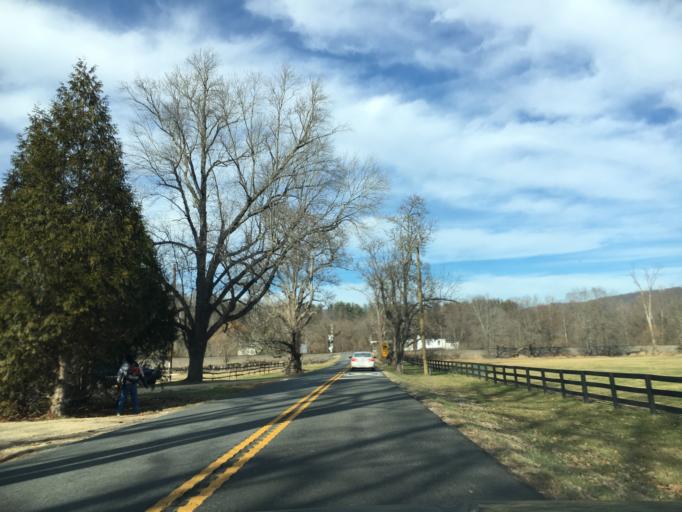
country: US
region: Virginia
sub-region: Warren County
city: Apple Mountain Lake
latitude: 38.9024
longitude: -78.0017
